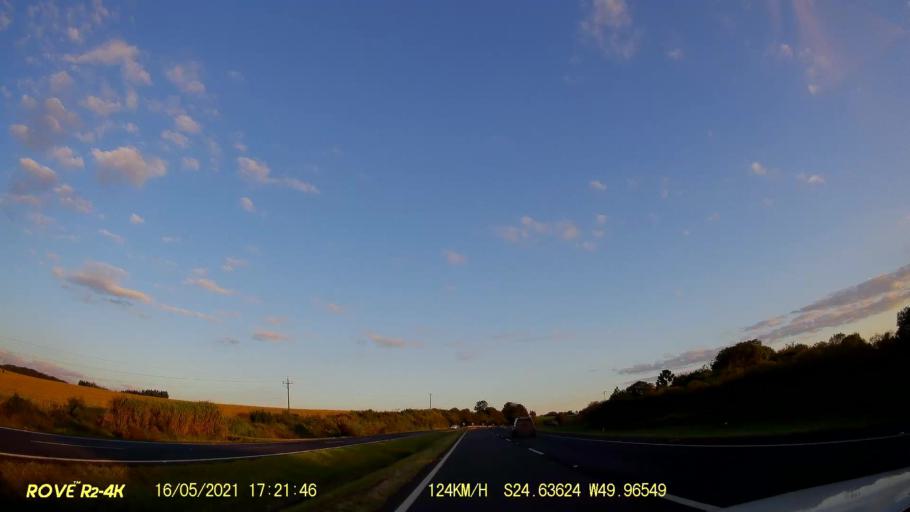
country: BR
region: Parana
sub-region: Pirai Do Sul
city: Pirai do Sul
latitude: -24.6366
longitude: -49.9655
